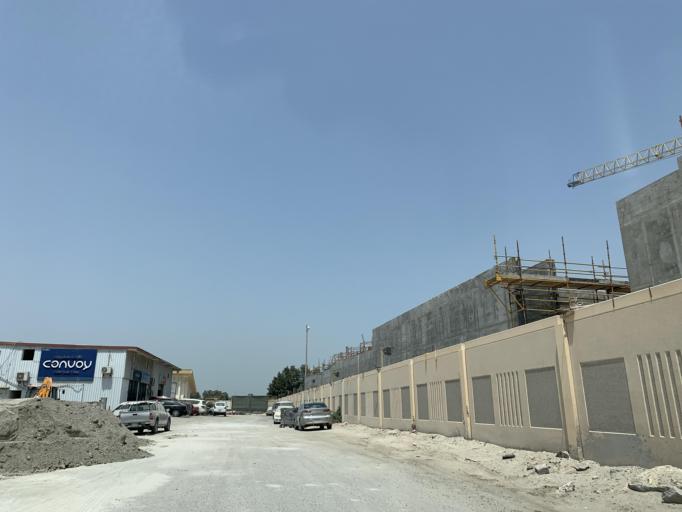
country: BH
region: Northern
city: Madinat `Isa
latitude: 26.1937
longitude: 50.5492
